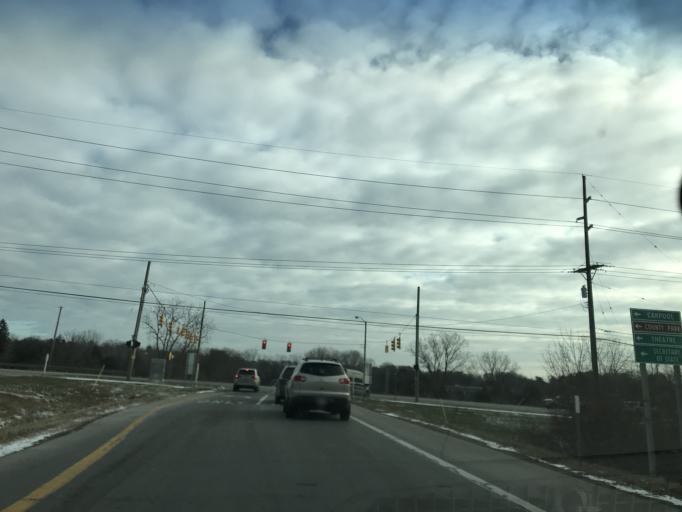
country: US
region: Michigan
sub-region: Oakland County
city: Clarkston
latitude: 42.7347
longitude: -83.3805
